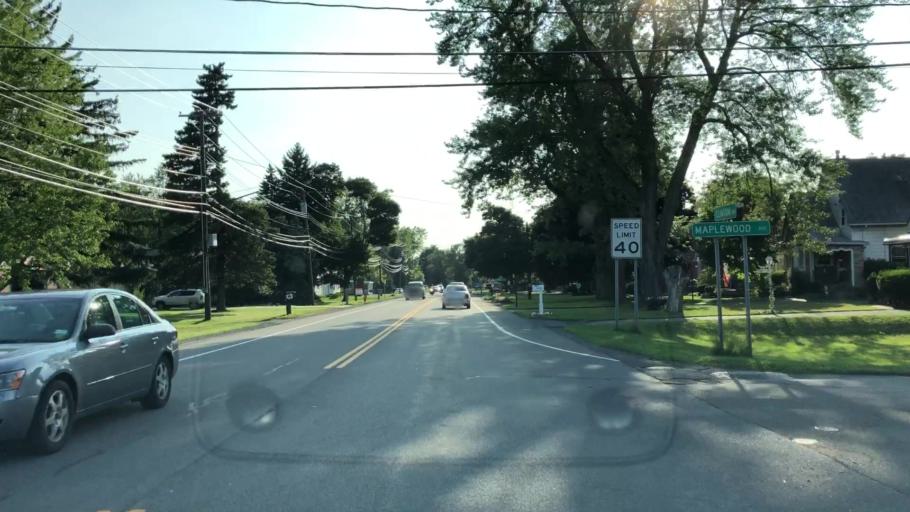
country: US
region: New York
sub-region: Erie County
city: Cheektowaga
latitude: 42.8561
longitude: -78.7460
